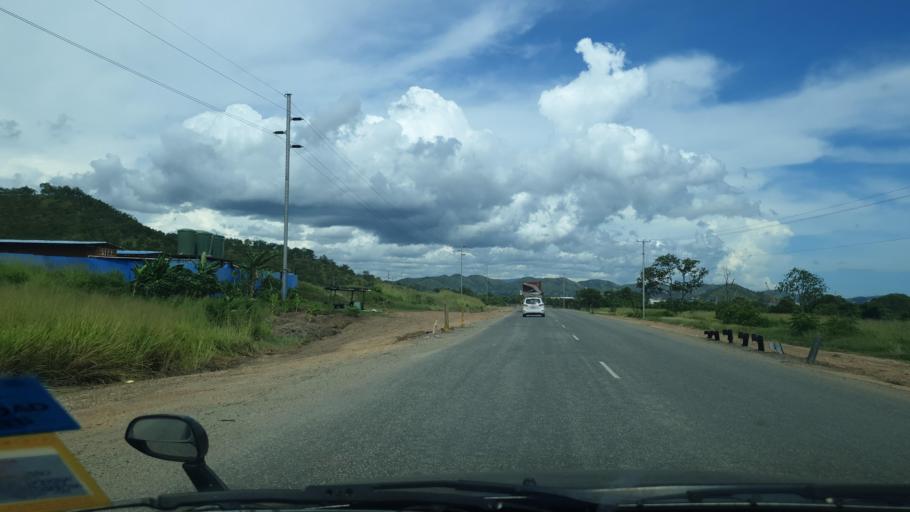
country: PG
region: National Capital
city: Port Moresby
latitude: -9.4194
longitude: 147.0898
